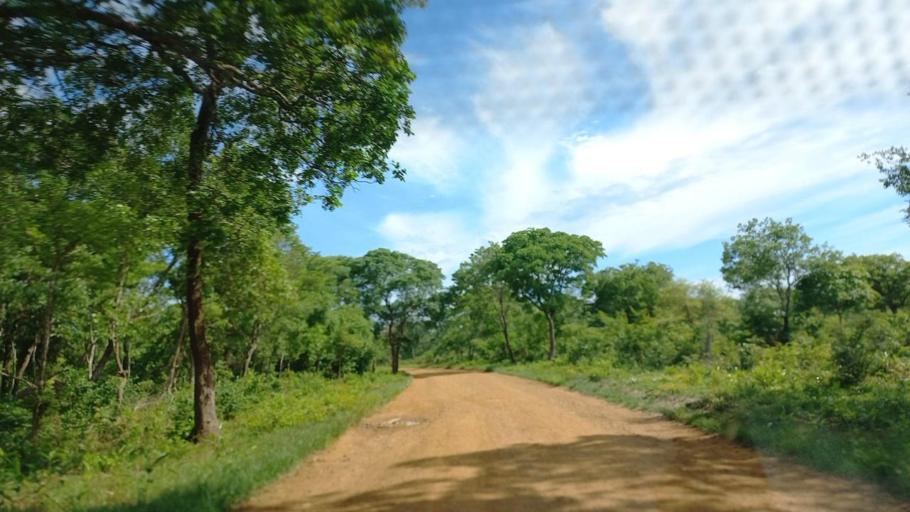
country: ZM
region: North-Western
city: Kabompo
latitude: -13.0866
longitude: 24.2202
